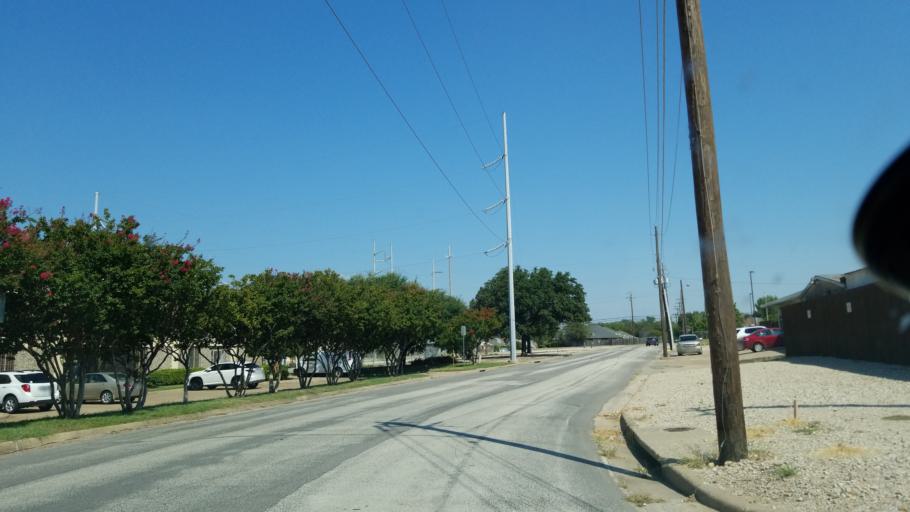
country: US
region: Texas
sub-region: Dallas County
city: Richardson
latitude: 32.9075
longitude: -96.7103
